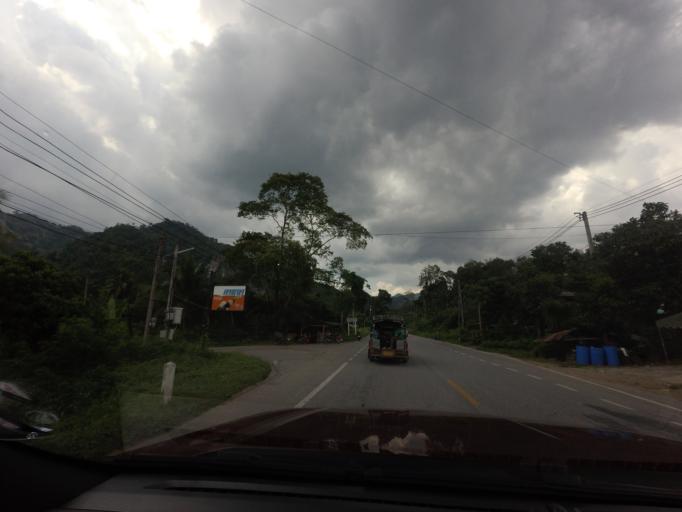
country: TH
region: Yala
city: Than To
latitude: 6.2222
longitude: 101.1654
